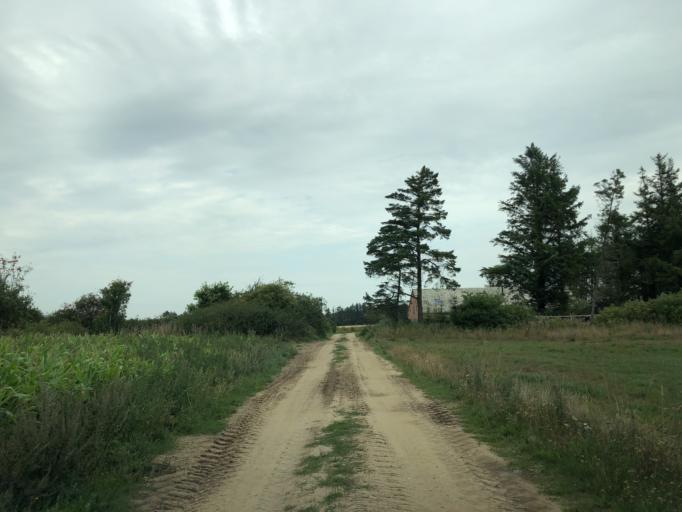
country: DK
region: Central Jutland
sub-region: Holstebro Kommune
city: Ulfborg
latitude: 56.2366
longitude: 8.3573
